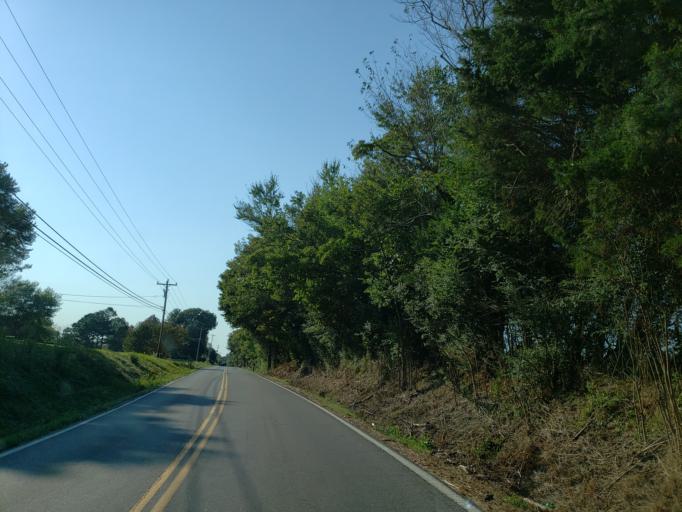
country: US
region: Tennessee
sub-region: Bradley County
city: Wildwood Lake
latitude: 35.1019
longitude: -84.8092
